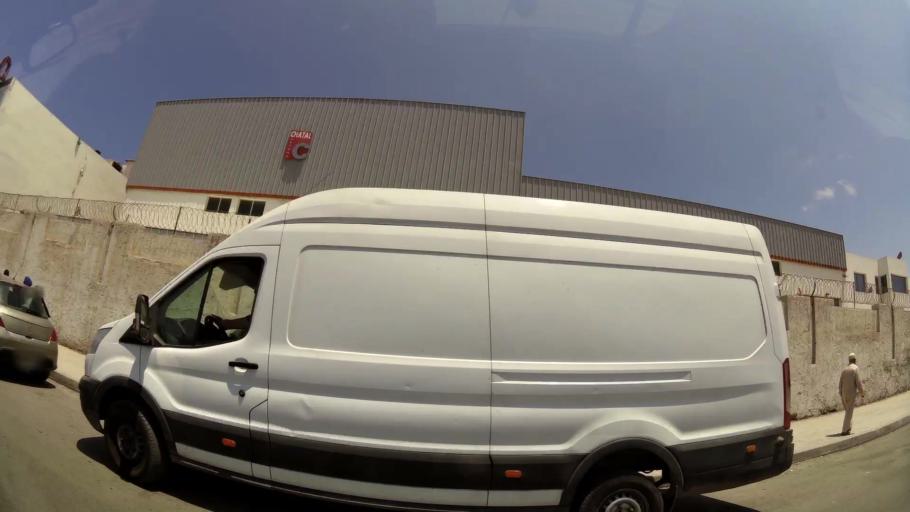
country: MA
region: Rabat-Sale-Zemmour-Zaer
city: Sale
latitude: 34.0561
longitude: -6.7962
